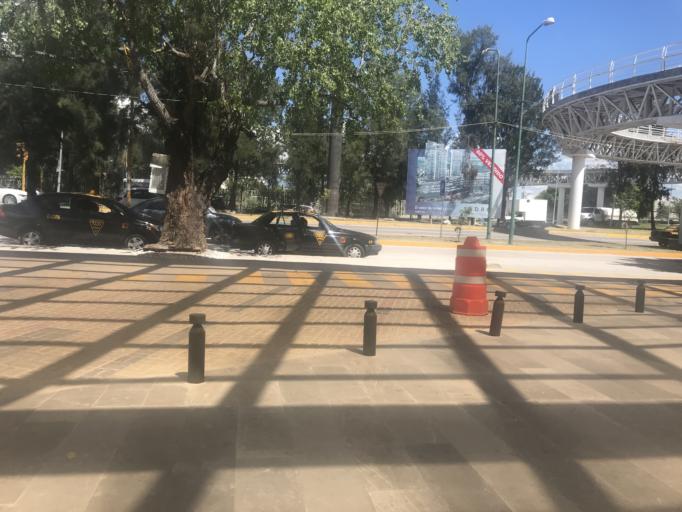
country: MX
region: Puebla
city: Puebla
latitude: 19.0327
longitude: -98.2415
